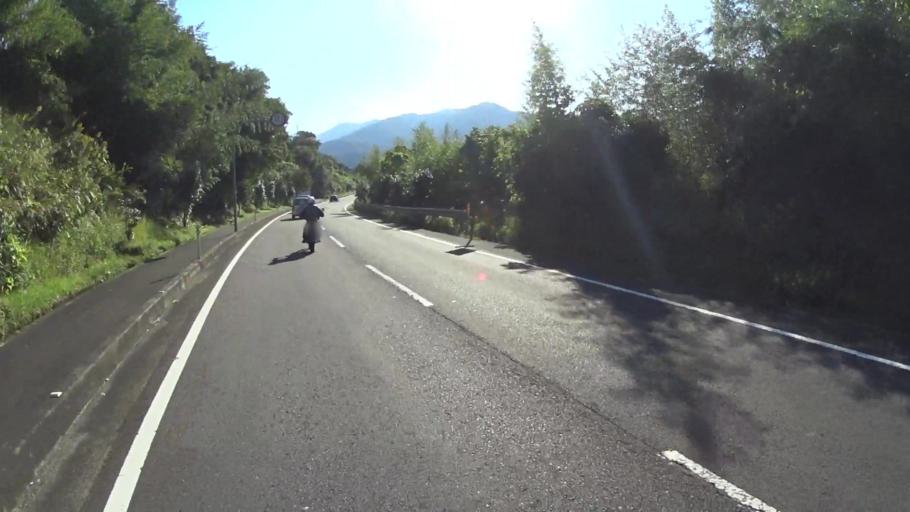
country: JP
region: Kyoto
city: Miyazu
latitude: 35.4884
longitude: 135.0973
